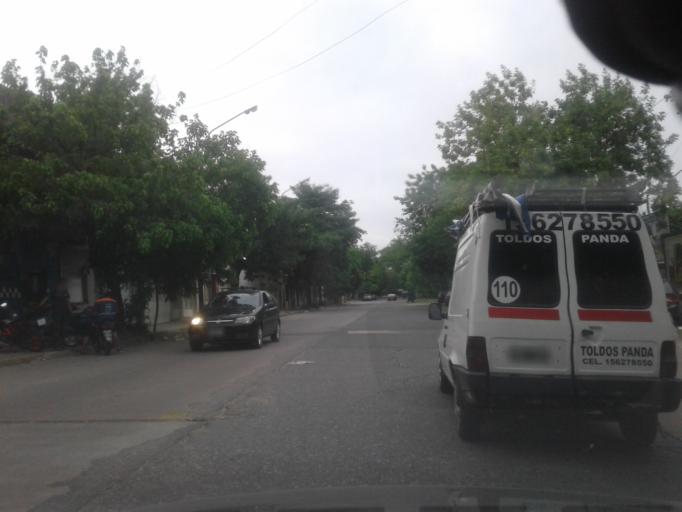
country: AR
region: Santa Fe
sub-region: Departamento de Rosario
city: Rosario
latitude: -32.9336
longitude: -60.6779
